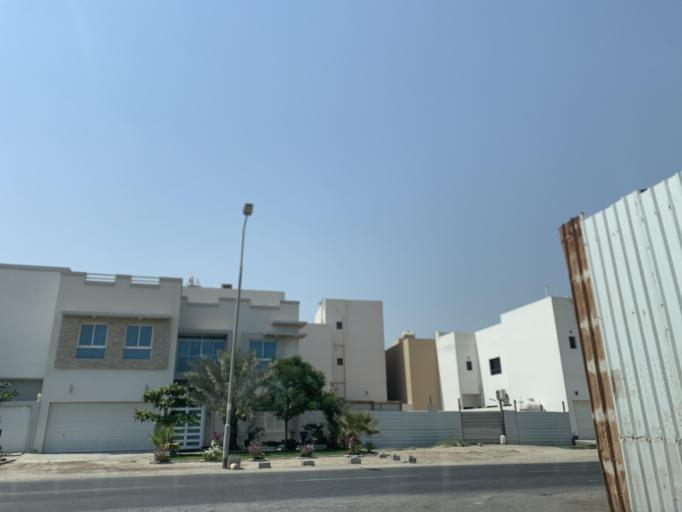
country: BH
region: Manama
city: Jidd Hafs
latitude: 26.2142
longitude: 50.5232
